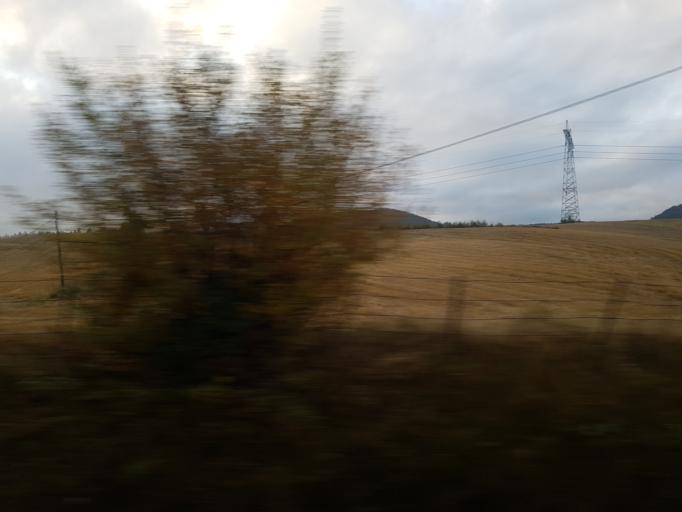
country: NO
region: Sor-Trondelag
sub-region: Melhus
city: Melhus
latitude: 63.3217
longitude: 10.3231
